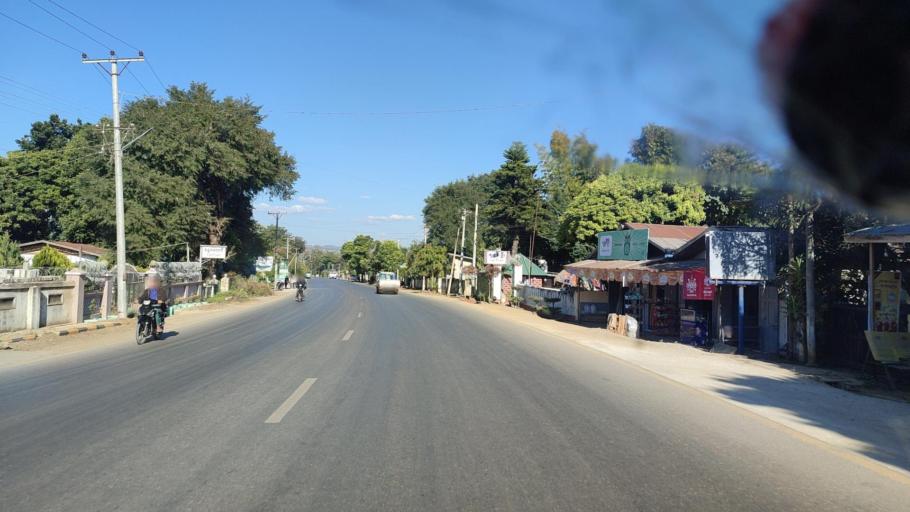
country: MM
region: Mandalay
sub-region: Pyin Oo Lwin District
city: Pyin Oo Lwin
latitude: 22.3333
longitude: 96.8079
